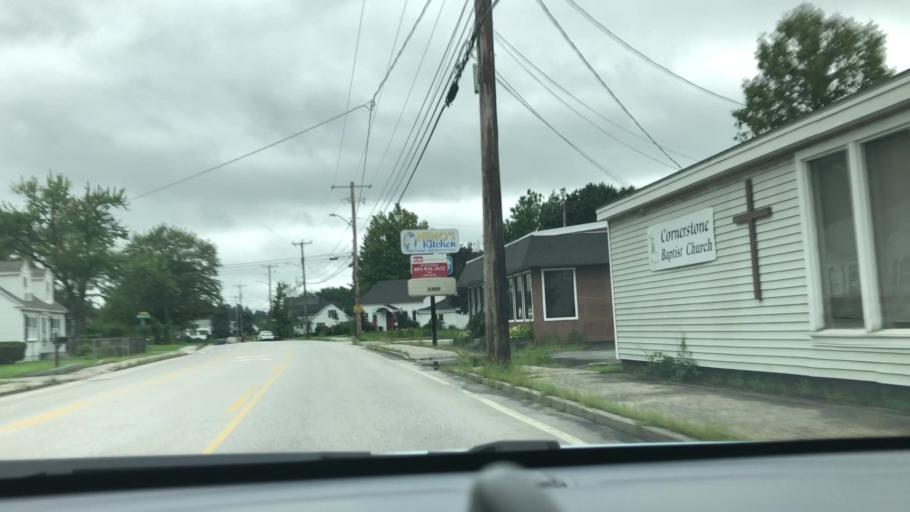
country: US
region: New Hampshire
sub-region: Hillsborough County
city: Pinardville
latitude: 42.9951
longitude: -71.5086
